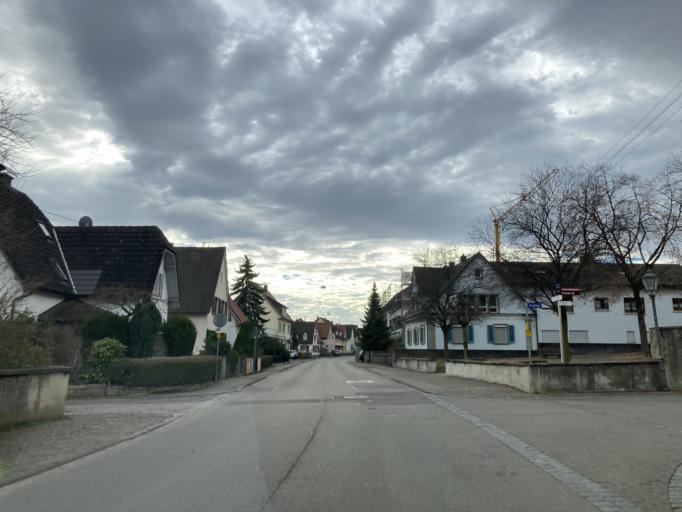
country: DE
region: Baden-Wuerttemberg
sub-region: Freiburg Region
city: Botzingen
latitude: 48.0741
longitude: 7.7225
